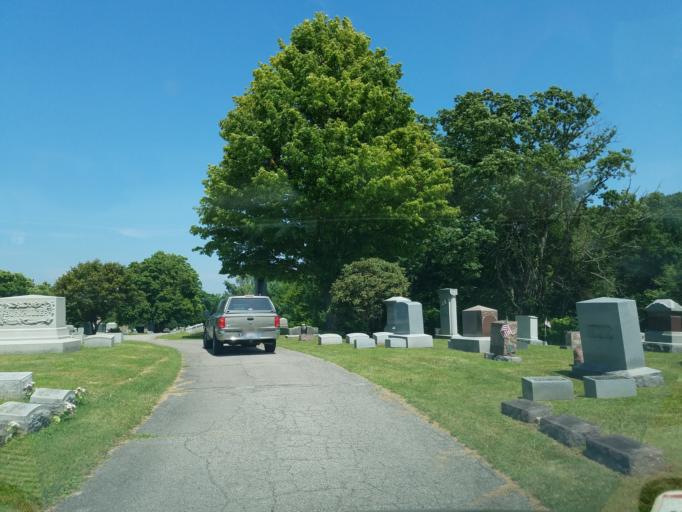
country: US
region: Ohio
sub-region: Ashland County
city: Ashland
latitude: 40.8659
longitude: -82.3279
